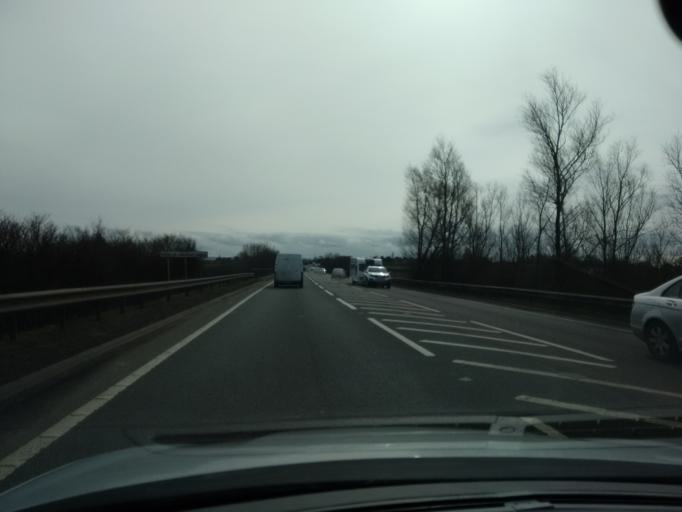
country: GB
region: England
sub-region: Worcestershire
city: Evesham
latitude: 52.1067
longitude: -1.9299
